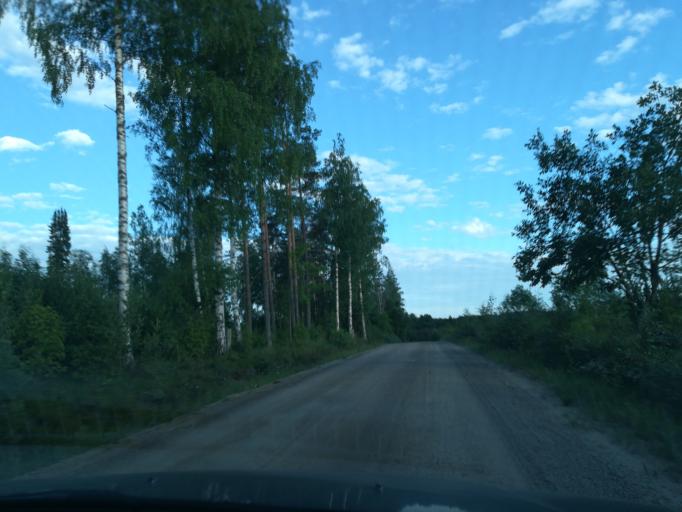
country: FI
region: Southern Savonia
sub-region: Mikkeli
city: Puumala
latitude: 61.6157
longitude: 28.1142
